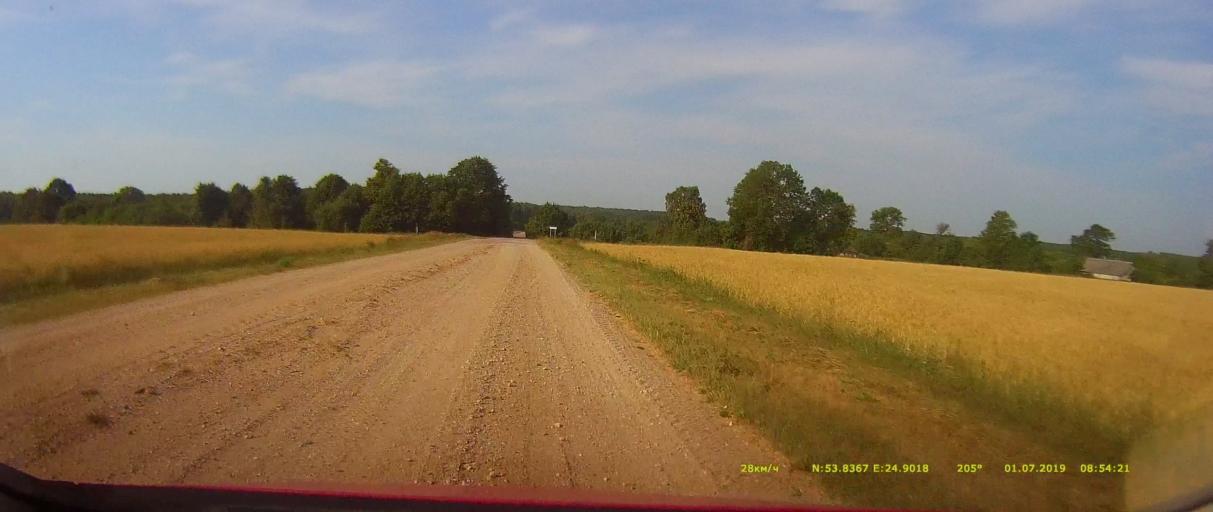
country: BY
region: Grodnenskaya
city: Shchuchin
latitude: 53.8368
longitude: 24.9019
